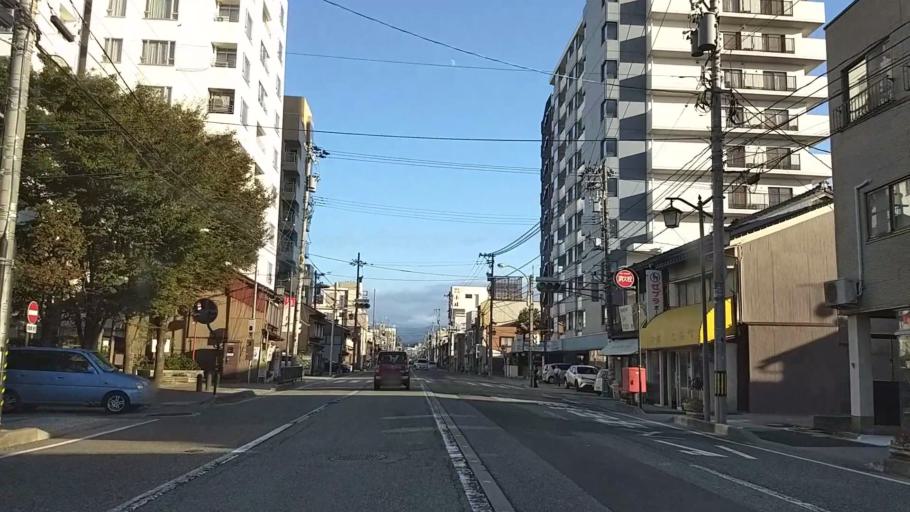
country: JP
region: Ishikawa
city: Nonoichi
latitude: 36.5515
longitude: 136.6546
